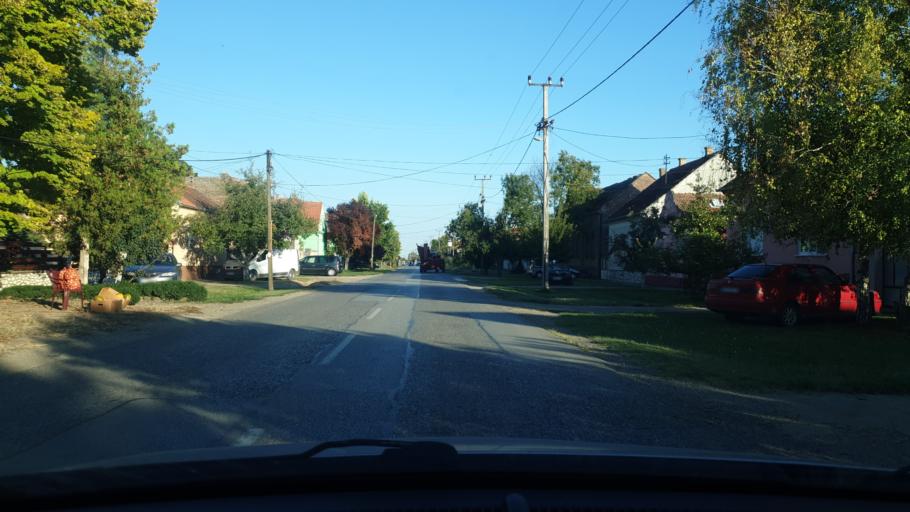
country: RS
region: Autonomna Pokrajina Vojvodina
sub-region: Sremski Okrug
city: Ruma
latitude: 44.9800
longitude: 19.8776
